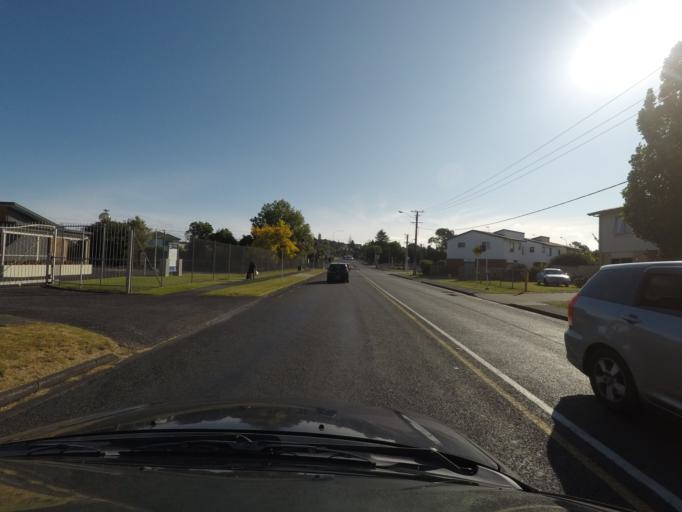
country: NZ
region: Auckland
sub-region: Auckland
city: Rosebank
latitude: -36.8677
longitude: 174.6062
